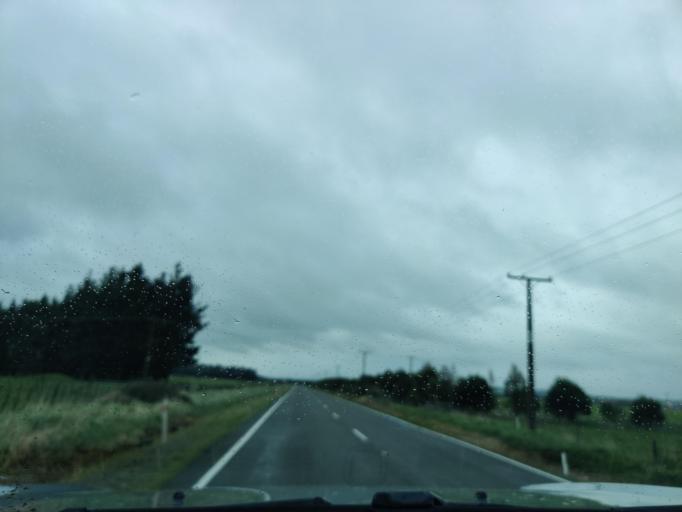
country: NZ
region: Hawke's Bay
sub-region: Hastings District
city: Hastings
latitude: -40.0083
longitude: 176.3820
